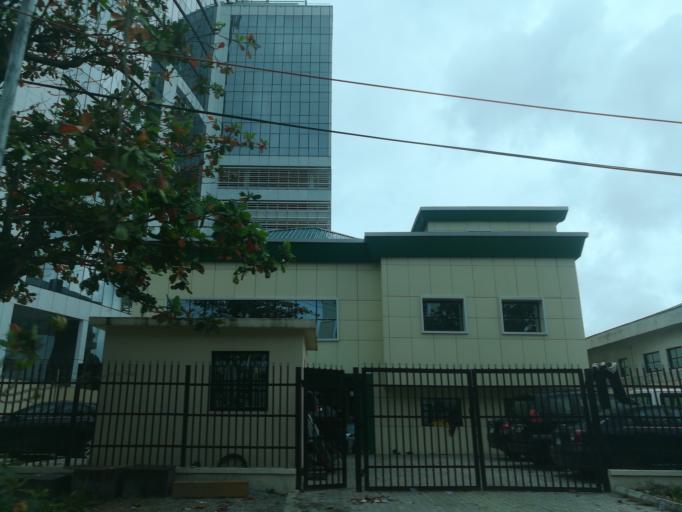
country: NG
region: Lagos
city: Ikoyi
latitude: 6.4270
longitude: 3.4233
